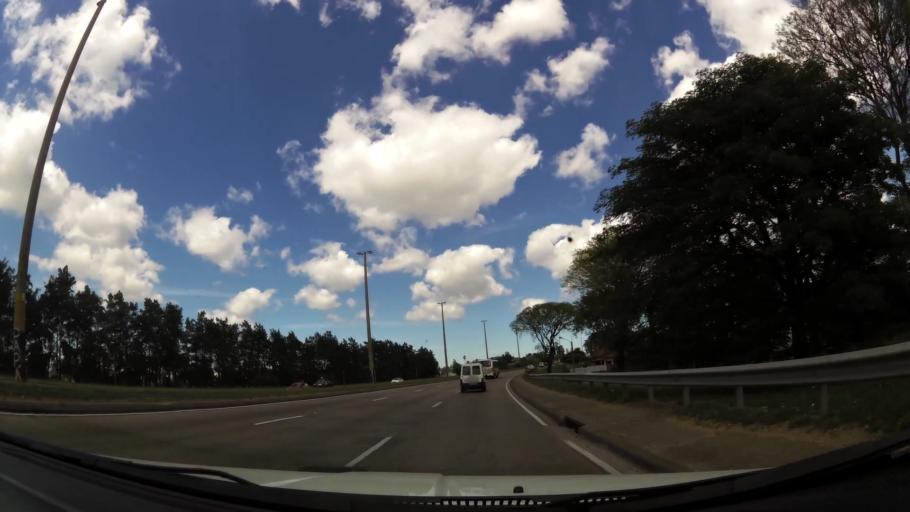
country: UY
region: Montevideo
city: Montevideo
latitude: -34.8706
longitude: -56.2284
